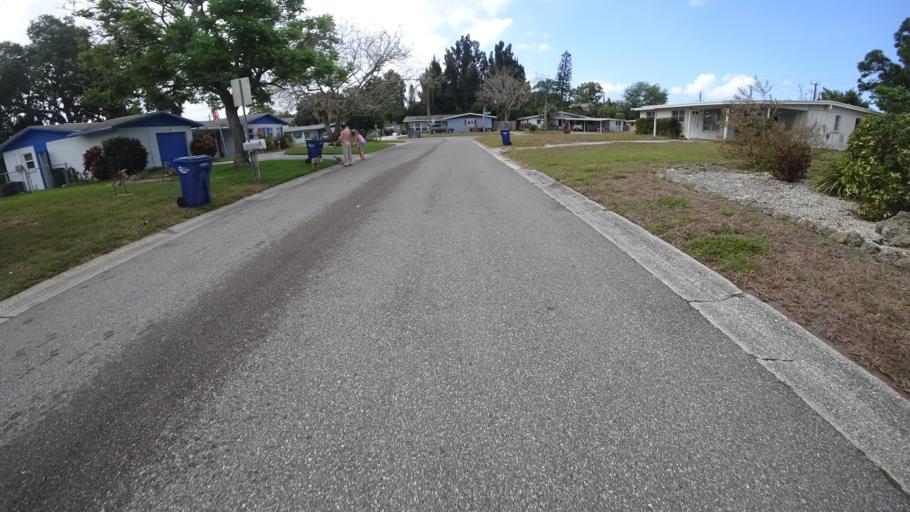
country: US
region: Florida
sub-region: Manatee County
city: Bayshore Gardens
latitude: 27.4376
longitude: -82.5869
